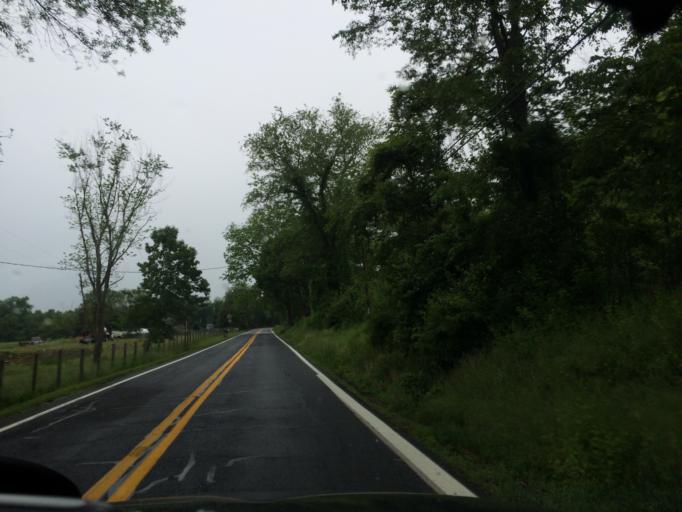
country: US
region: Maryland
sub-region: Frederick County
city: Thurmont
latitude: 39.6115
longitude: -77.3403
